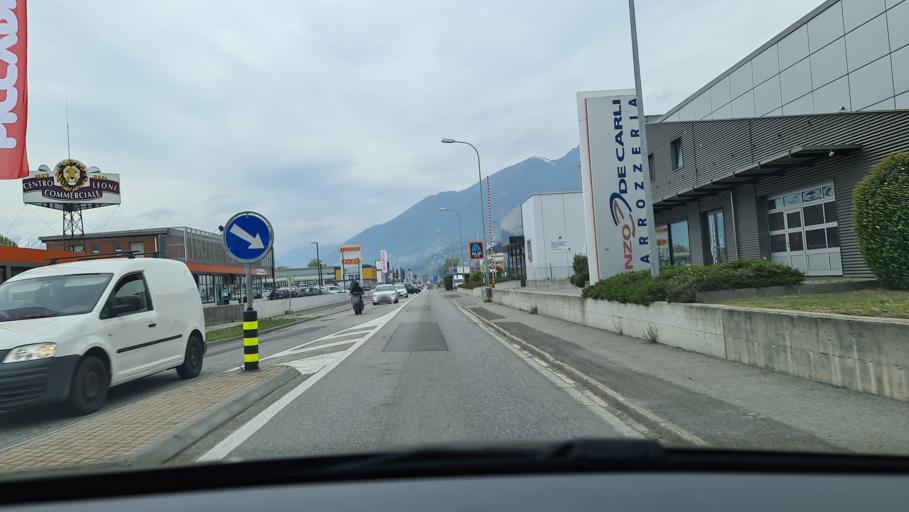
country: CH
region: Ticino
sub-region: Locarno District
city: Gordola
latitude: 46.1754
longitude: 8.8914
